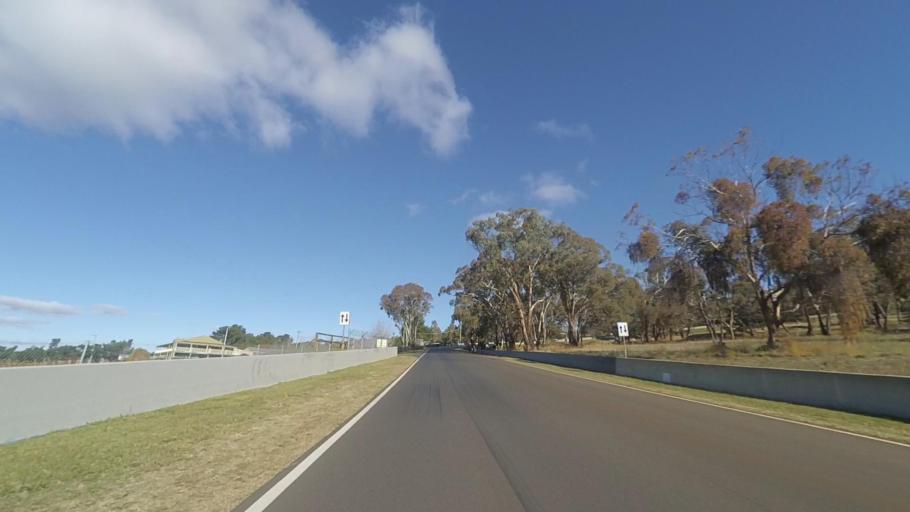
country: AU
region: New South Wales
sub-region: Bathurst Regional
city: Bathurst
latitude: -33.4474
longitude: 149.5540
